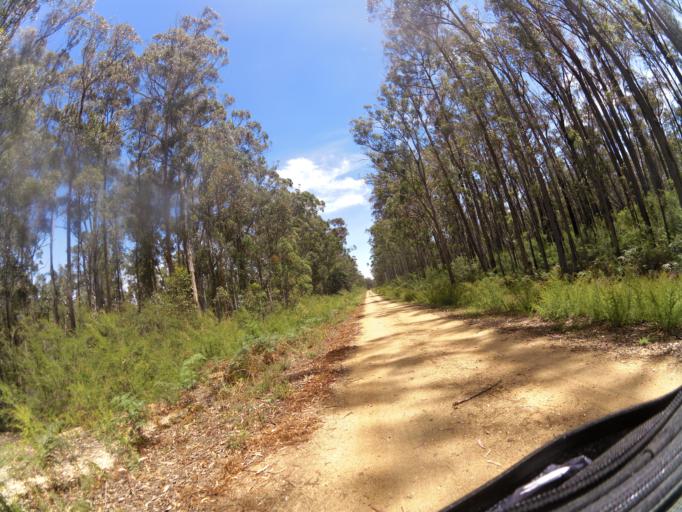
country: AU
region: Victoria
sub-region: East Gippsland
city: Lakes Entrance
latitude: -37.7575
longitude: 147.9610
